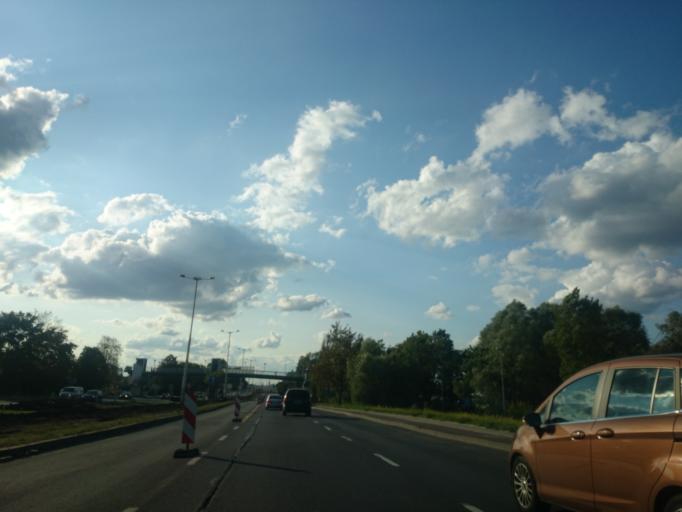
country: PL
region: West Pomeranian Voivodeship
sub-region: Szczecin
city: Szczecin
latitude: 53.4044
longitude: 14.5965
